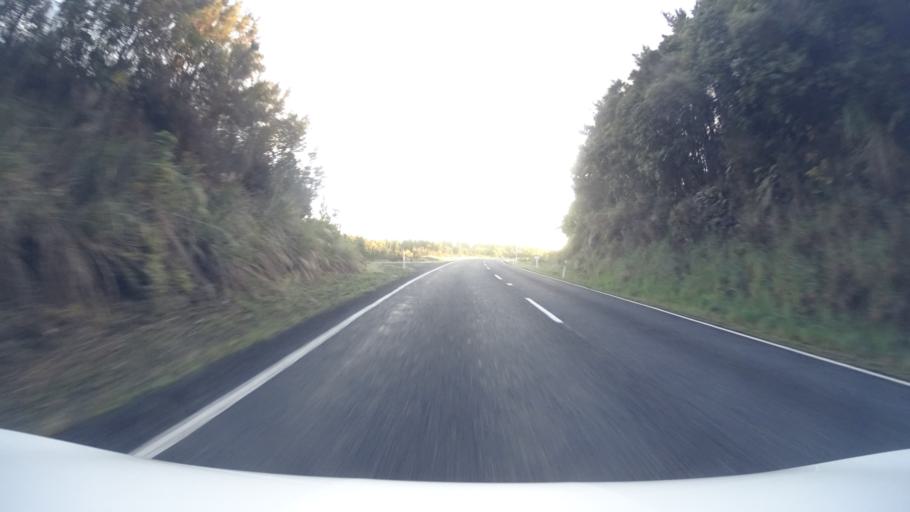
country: NZ
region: Waikato
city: Turangi
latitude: -39.0629
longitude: 175.6396
